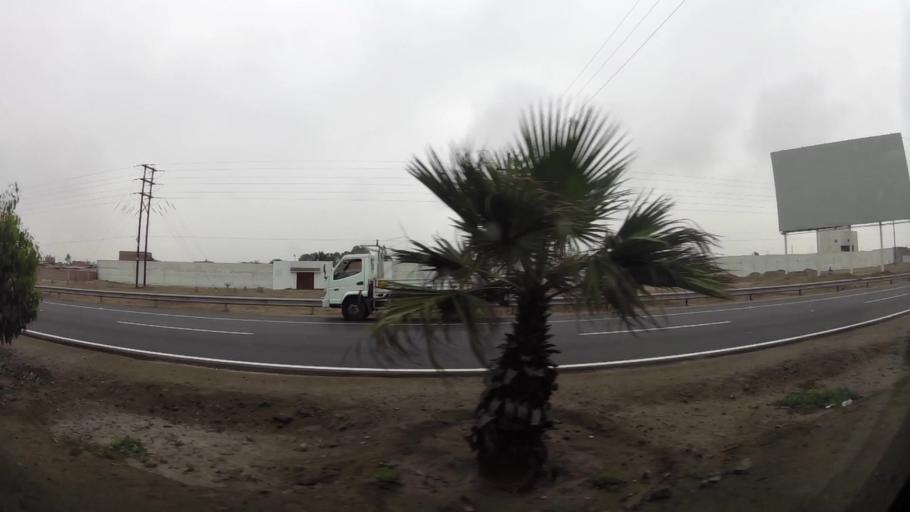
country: PE
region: Lima
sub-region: Lima
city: Punta Hermosa
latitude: -12.3108
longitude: -76.8351
